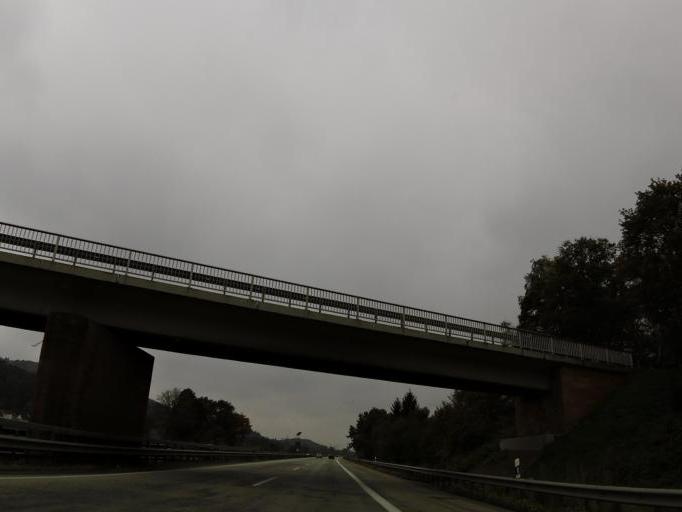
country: DE
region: Rheinland-Pfalz
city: Bruchmuhlbach-Miesau
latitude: 49.3821
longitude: 7.4231
